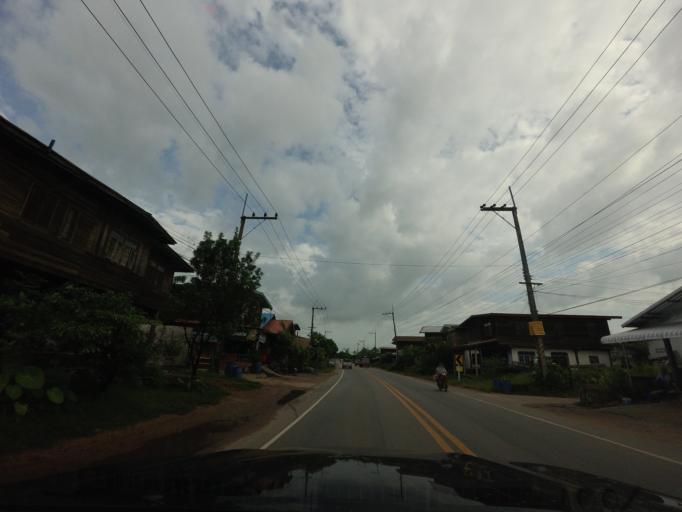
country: TH
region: Changwat Udon Thani
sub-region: Amphoe Ban Phue
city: Ban Phue
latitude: 17.7489
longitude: 102.3993
